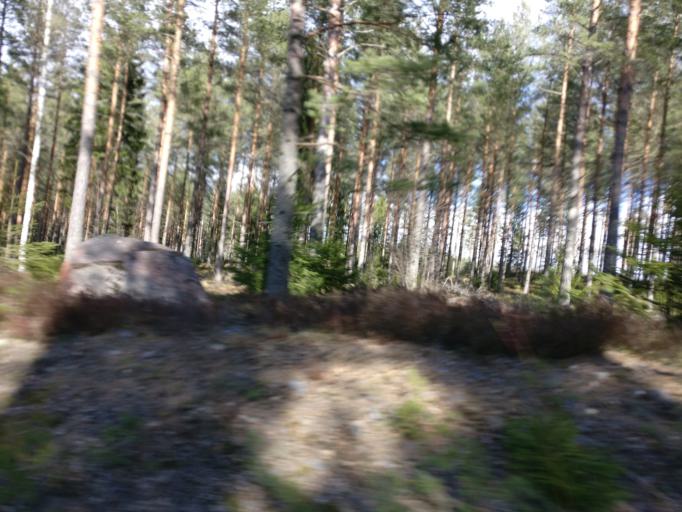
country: FI
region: Uusimaa
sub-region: Helsinki
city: Sammatti
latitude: 60.2766
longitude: 23.7784
